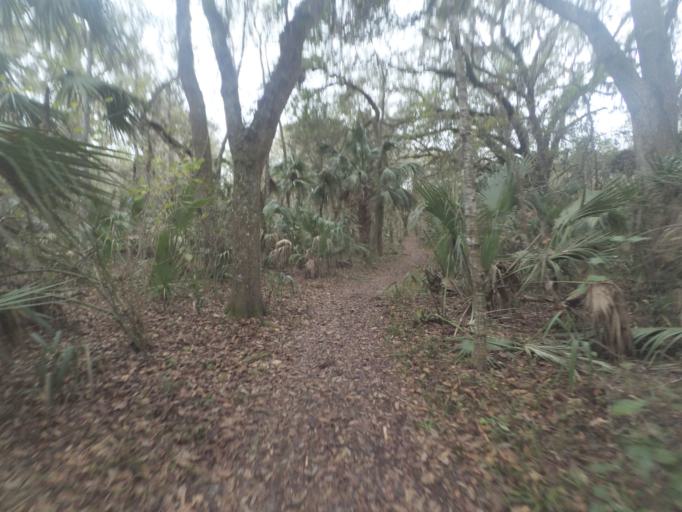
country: US
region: Florida
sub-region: Alachua County
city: Gainesville
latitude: 29.5494
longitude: -82.2937
